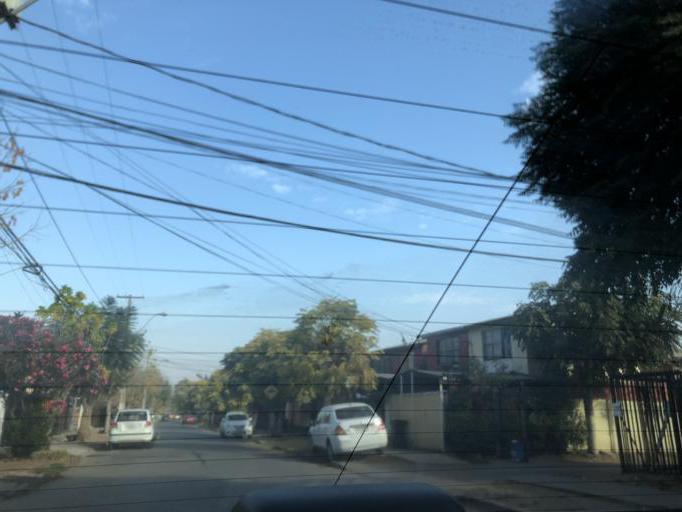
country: CL
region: Santiago Metropolitan
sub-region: Provincia de Cordillera
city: Puente Alto
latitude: -33.5896
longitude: -70.5635
